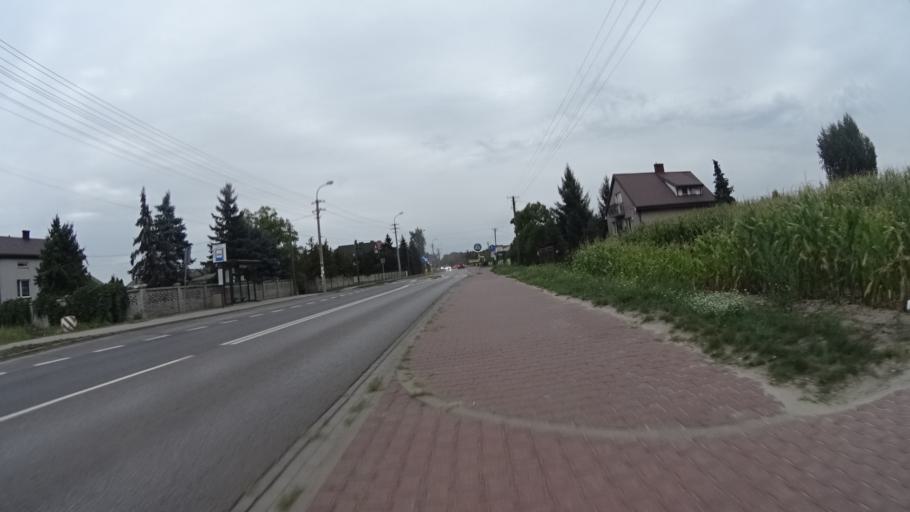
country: PL
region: Masovian Voivodeship
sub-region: Powiat warszawski zachodni
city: Stare Babice
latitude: 52.2533
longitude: 20.8042
